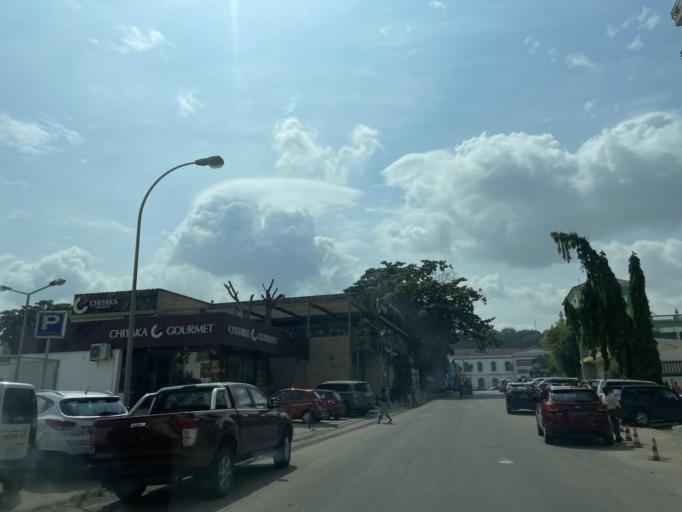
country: AO
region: Luanda
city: Luanda
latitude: -8.8040
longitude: 13.2434
